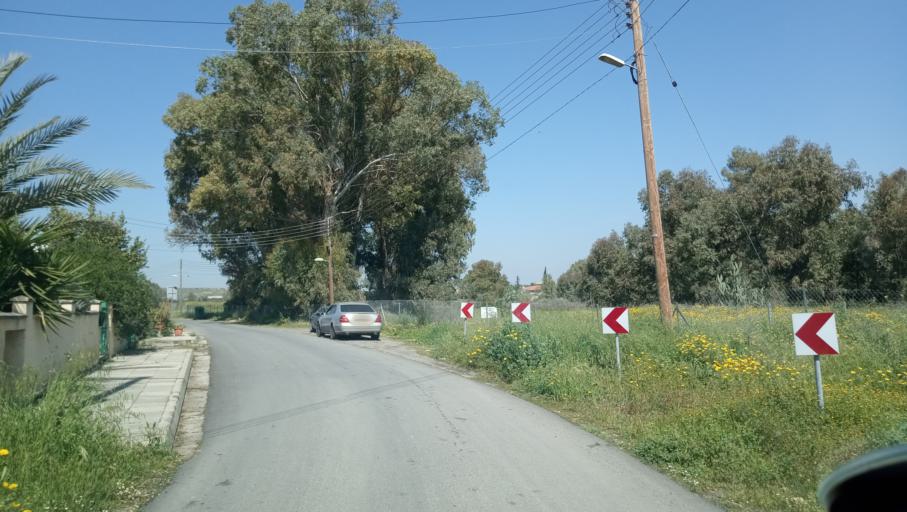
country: CY
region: Lefkosia
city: Alampra
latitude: 35.0153
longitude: 33.3868
